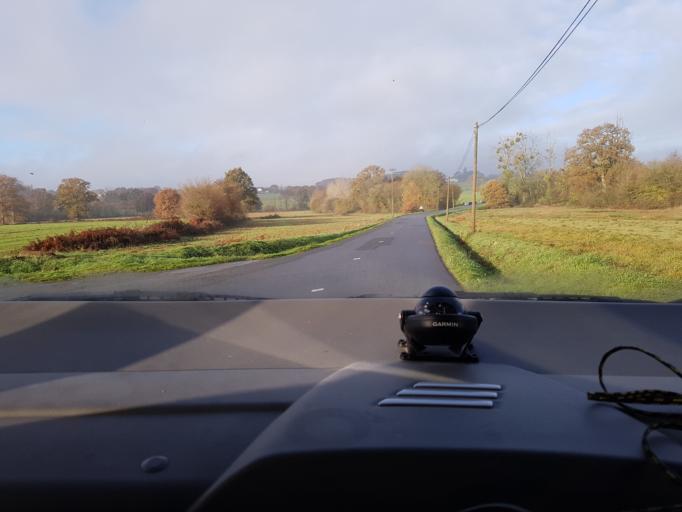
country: FR
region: Brittany
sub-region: Departement d'Ille-et-Vilaine
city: Liffre
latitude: 48.1821
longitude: -1.4963
